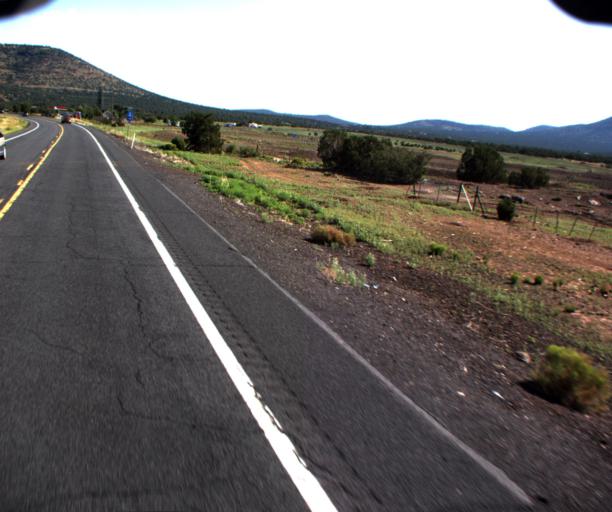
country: US
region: Arizona
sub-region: Coconino County
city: Williams
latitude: 35.3756
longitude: -112.1621
